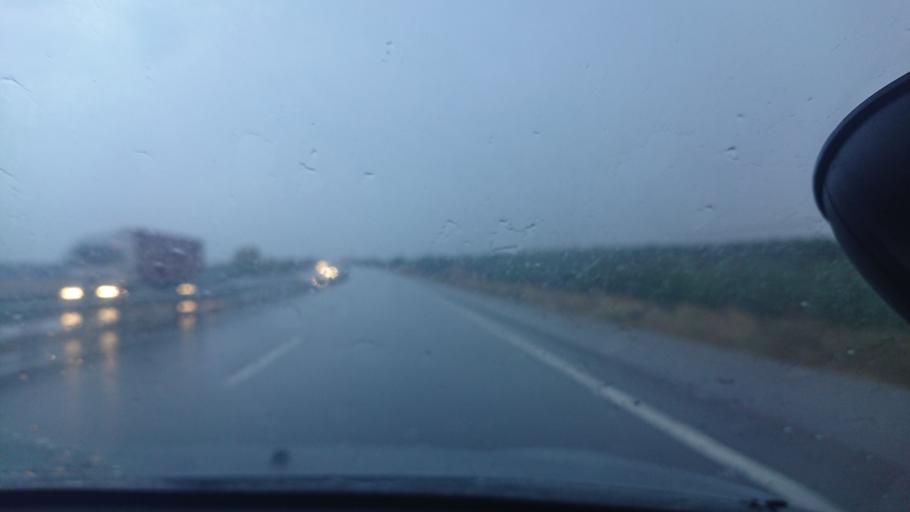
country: TR
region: Manisa
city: Menye
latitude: 38.5298
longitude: 28.3938
